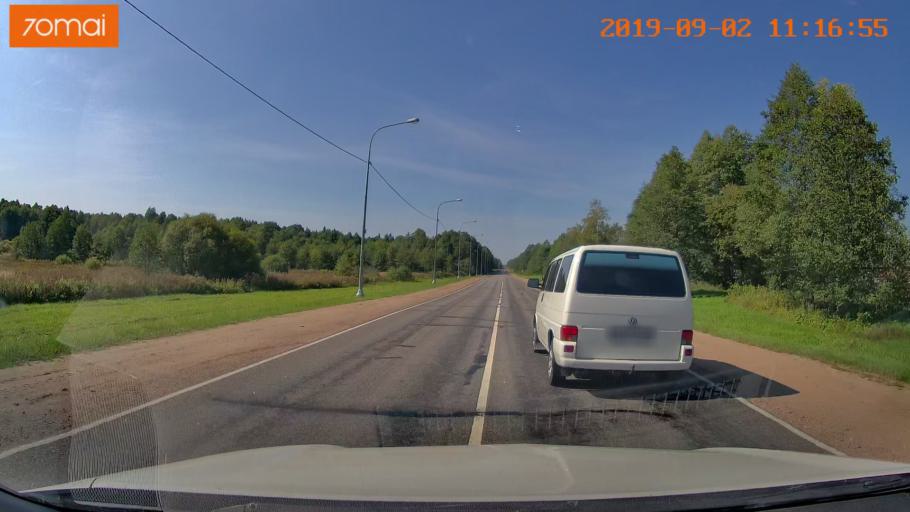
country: RU
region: Smolensk
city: Yekimovichi
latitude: 54.0650
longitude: 33.1295
